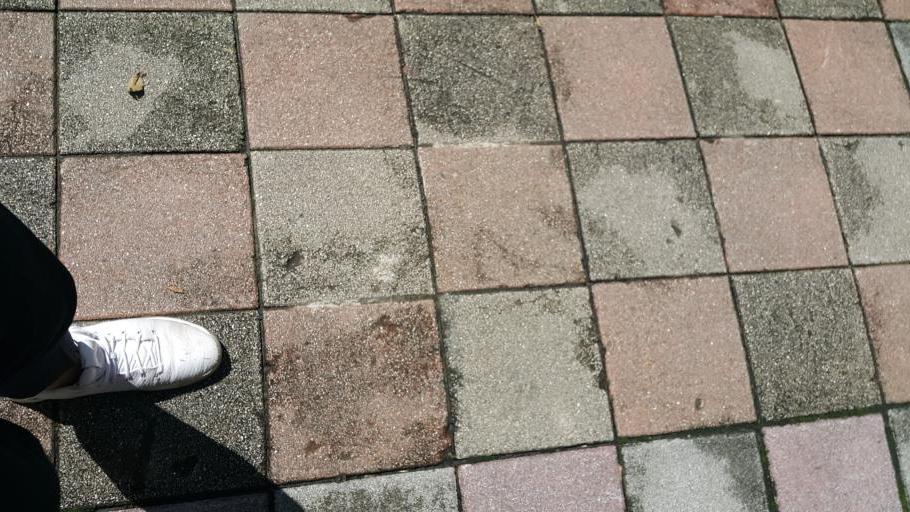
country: TW
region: Taipei
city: Taipei
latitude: 24.9745
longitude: 121.5296
